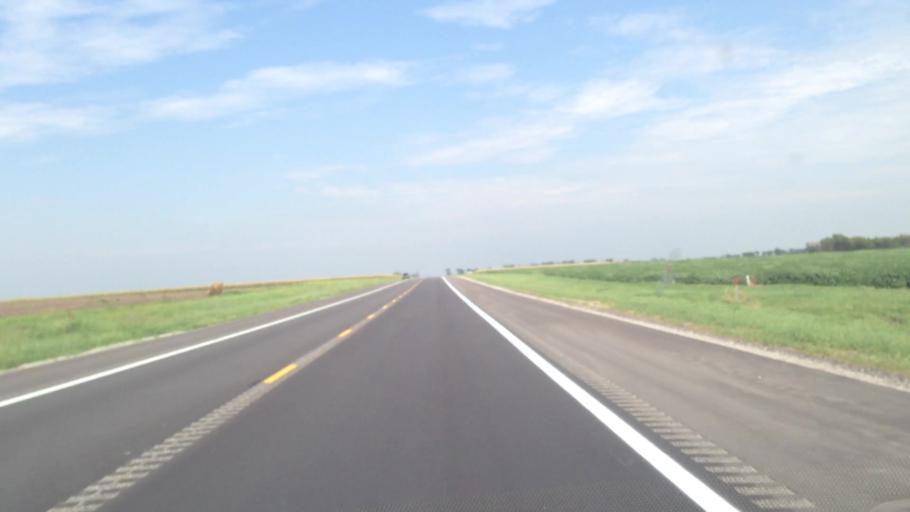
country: US
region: Kansas
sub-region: Anderson County
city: Garnett
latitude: 38.4381
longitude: -95.2487
